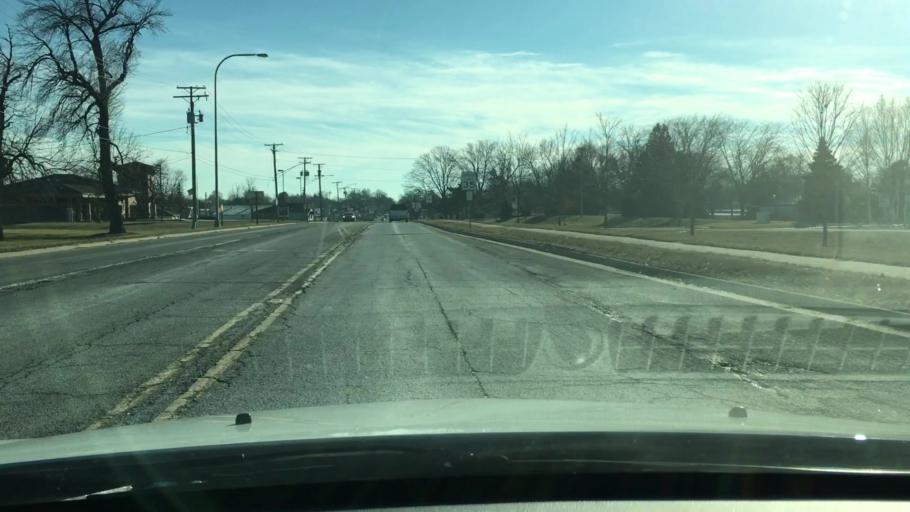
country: US
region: Illinois
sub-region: LaSalle County
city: Mendota
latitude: 41.5614
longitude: -89.1279
